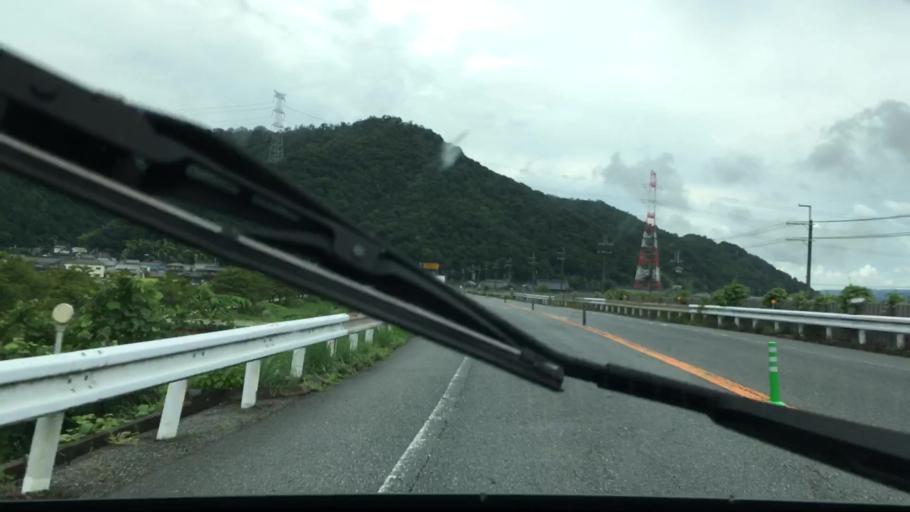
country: JP
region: Hyogo
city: Himeji
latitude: 34.9763
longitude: 134.7687
